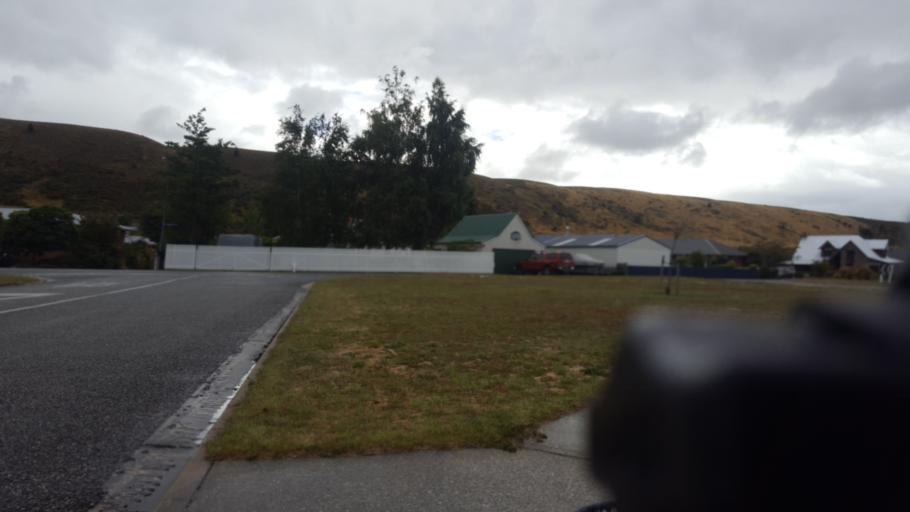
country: NZ
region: Otago
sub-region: Queenstown-Lakes District
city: Wanaka
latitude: -45.1926
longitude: 169.3296
